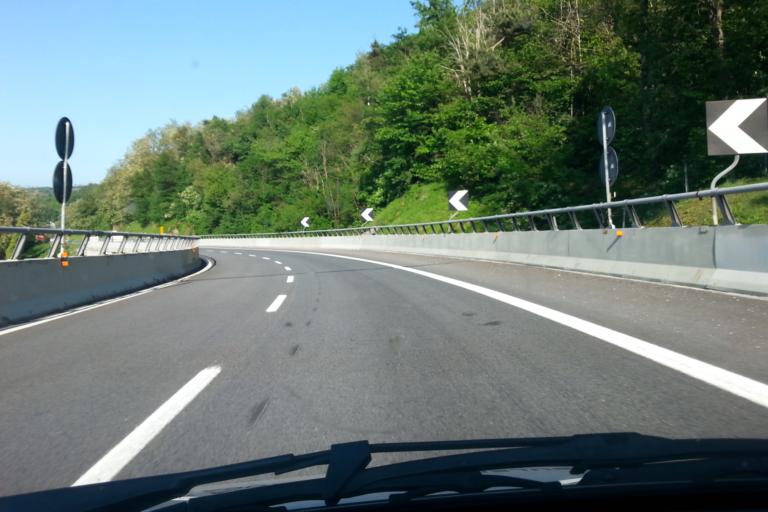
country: IT
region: Liguria
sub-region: Provincia di Savona
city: Roccavignale
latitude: 44.3576
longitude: 8.1849
